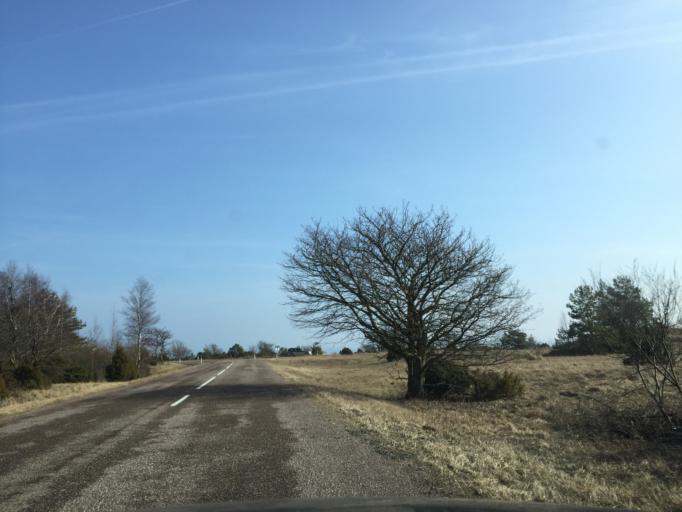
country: LV
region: Dundaga
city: Dundaga
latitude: 57.9184
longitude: 22.0621
